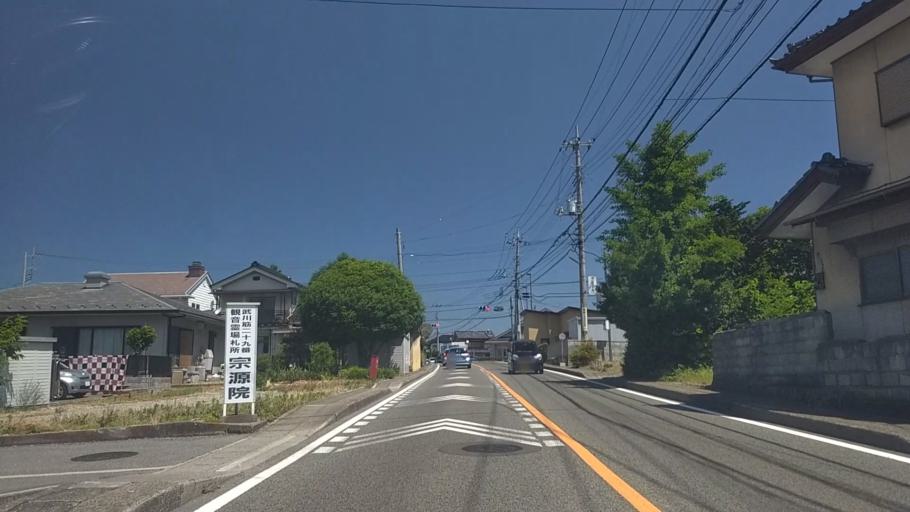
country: JP
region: Yamanashi
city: Nirasaki
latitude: 35.6775
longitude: 138.4649
